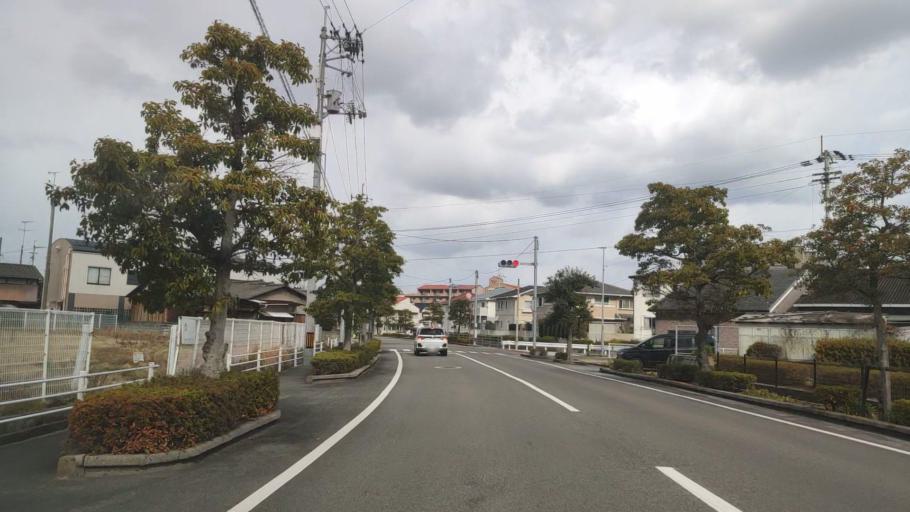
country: JP
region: Ehime
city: Saijo
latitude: 34.0614
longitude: 133.0119
